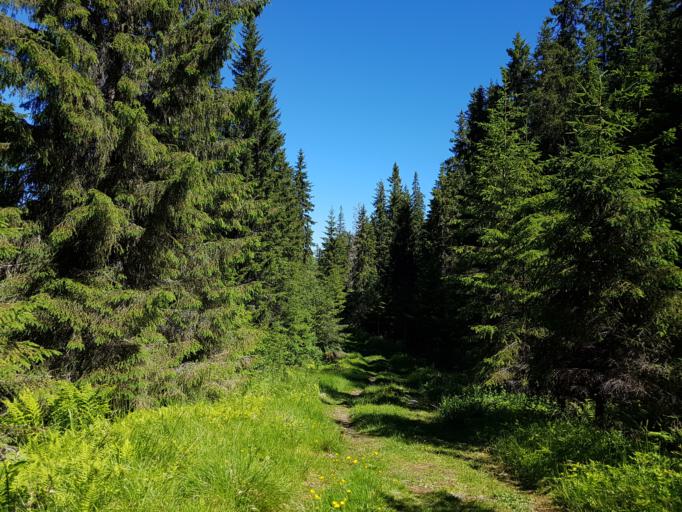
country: NO
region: Sor-Trondelag
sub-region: Melhus
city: Melhus
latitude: 63.4342
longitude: 10.2027
